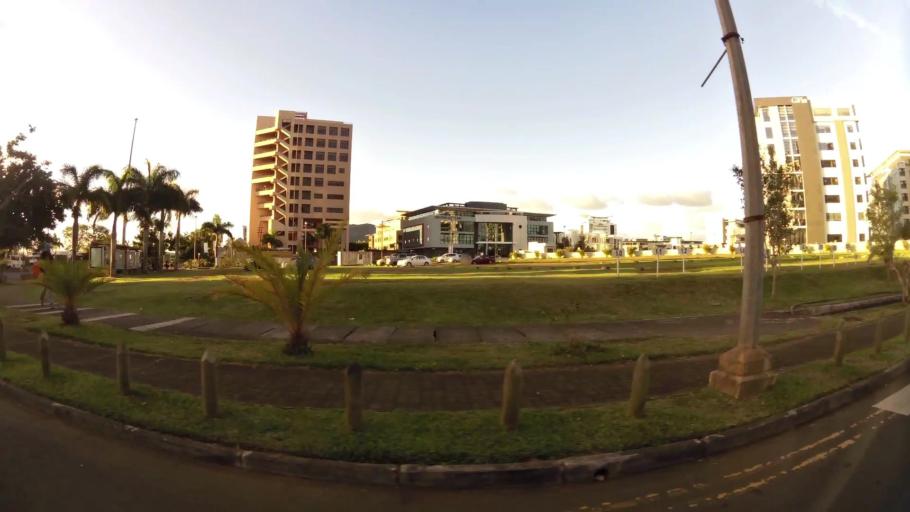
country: MU
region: Plaines Wilhems
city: Ebene
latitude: -20.2441
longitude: 57.4920
